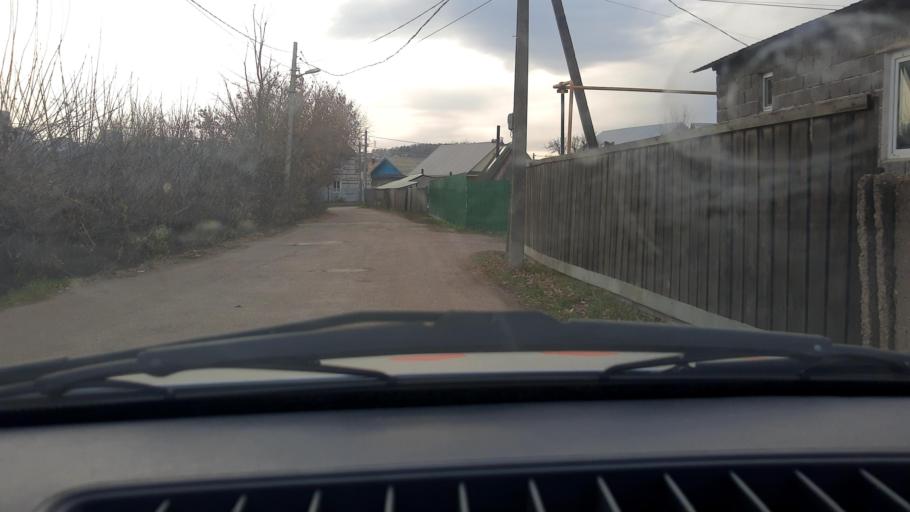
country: RU
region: Bashkortostan
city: Ufa
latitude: 54.7380
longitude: 55.9060
